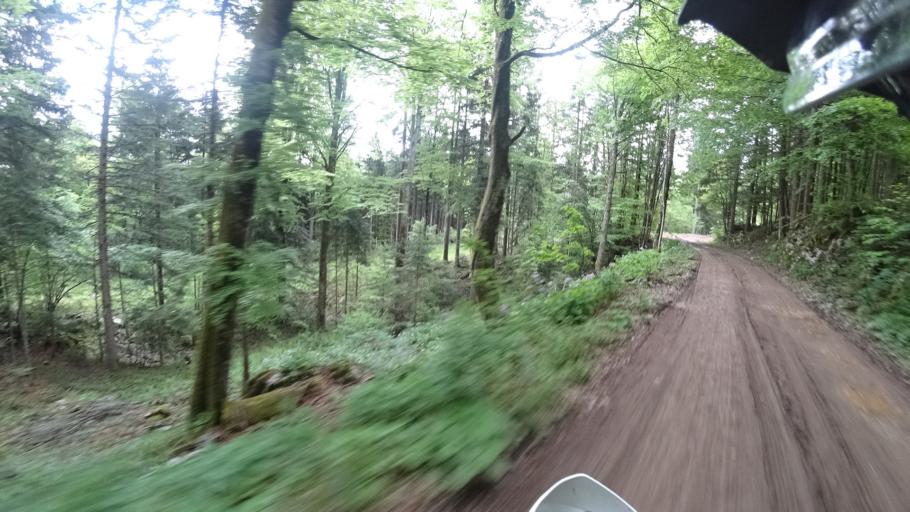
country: HR
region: Karlovacka
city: Plaski
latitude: 44.9606
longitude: 15.4085
